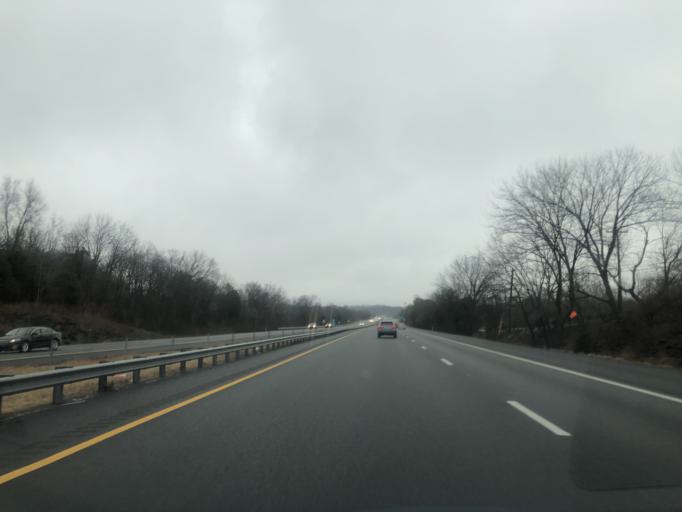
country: US
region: Tennessee
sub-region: Cheatham County
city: Pegram
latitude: 36.0770
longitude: -86.9671
